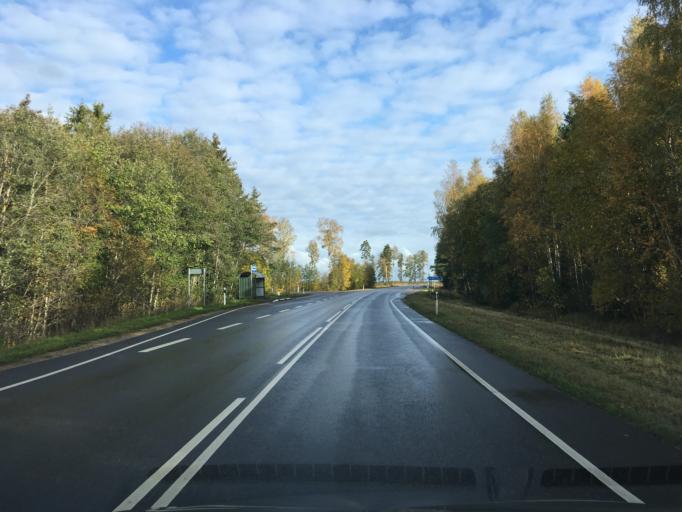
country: EE
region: Harju
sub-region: Raasiku vald
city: Raasiku
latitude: 59.2058
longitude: 25.1848
